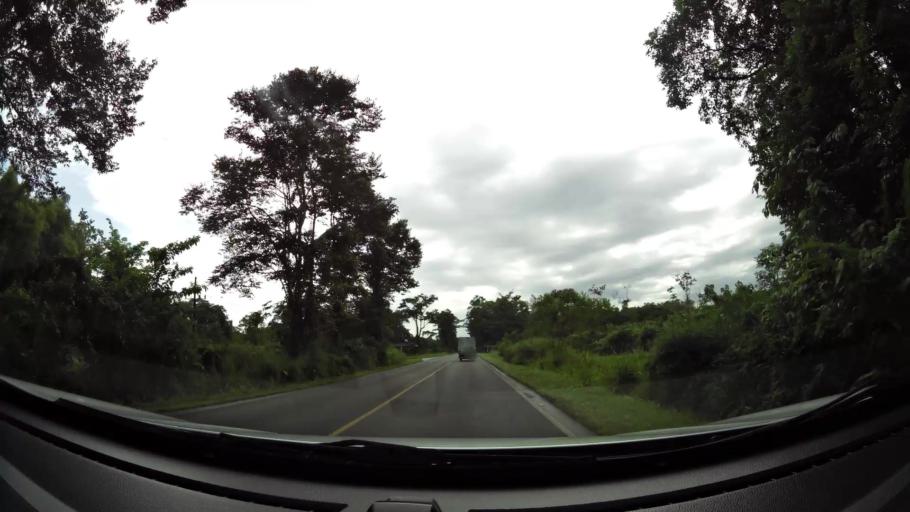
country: CR
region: Limon
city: Pocora
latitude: 10.1808
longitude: -83.6237
